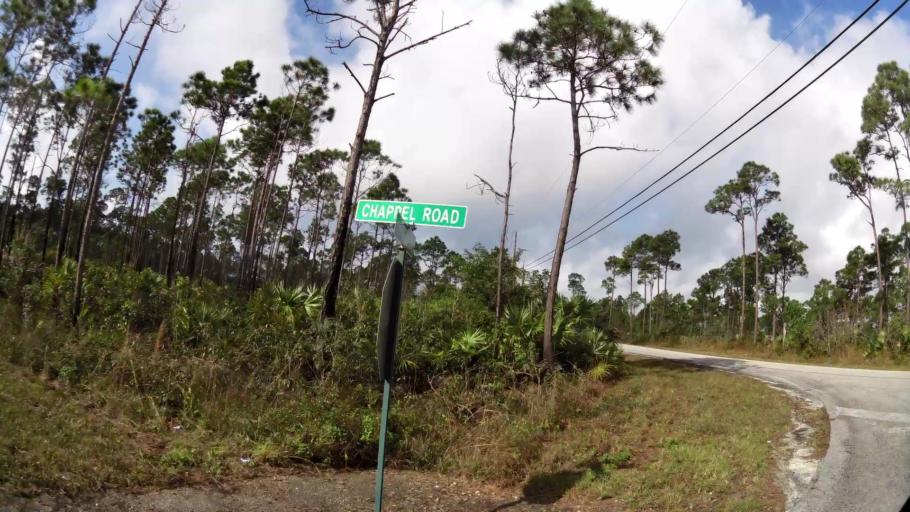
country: BS
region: Freeport
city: Lucaya
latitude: 26.5707
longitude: -78.5855
